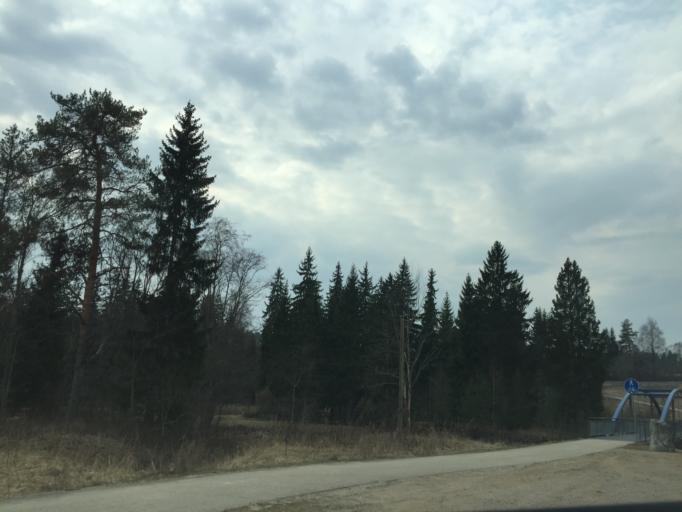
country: LV
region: Amatas Novads
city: Drabesi
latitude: 57.2216
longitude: 25.2363
